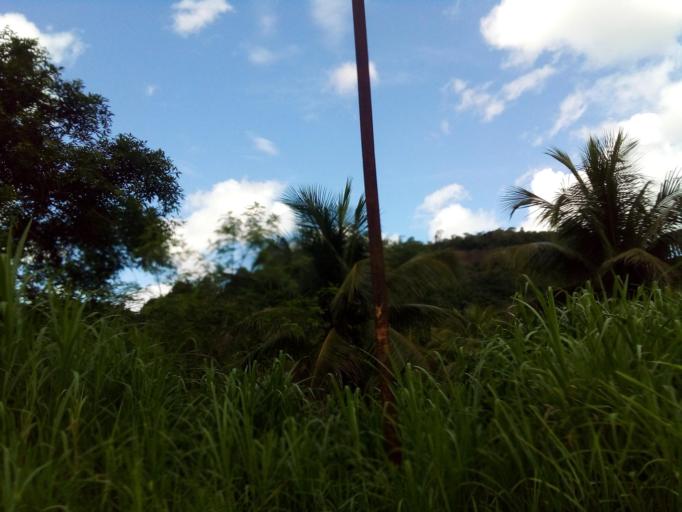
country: BR
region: Espirito Santo
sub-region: Ibiracu
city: Ibiracu
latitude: -19.8669
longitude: -40.3615
